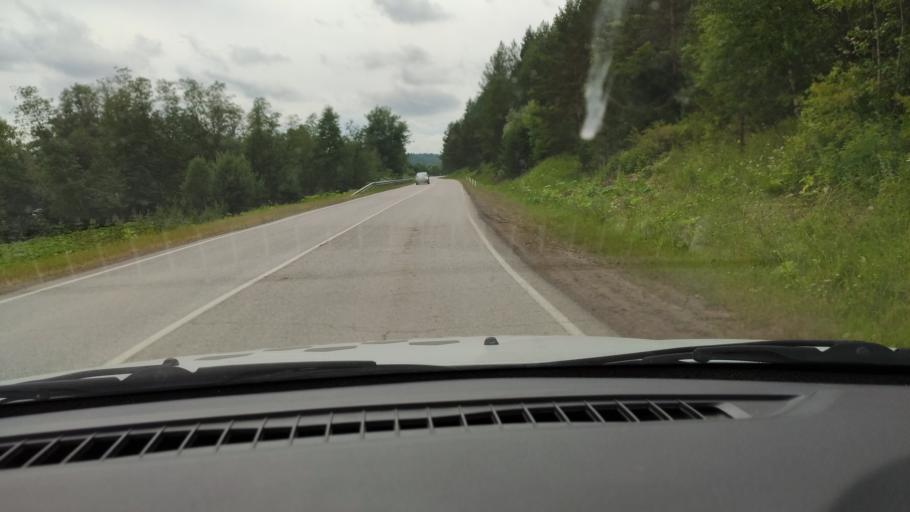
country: RU
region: Perm
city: Kukushtan
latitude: 57.4945
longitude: 56.6427
